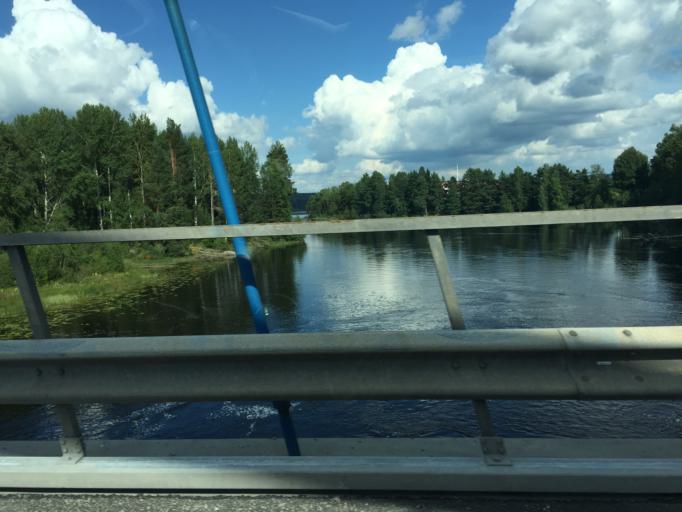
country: SE
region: Gaevleborg
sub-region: Bollnas Kommun
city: Bollnas
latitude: 61.3156
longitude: 16.4398
